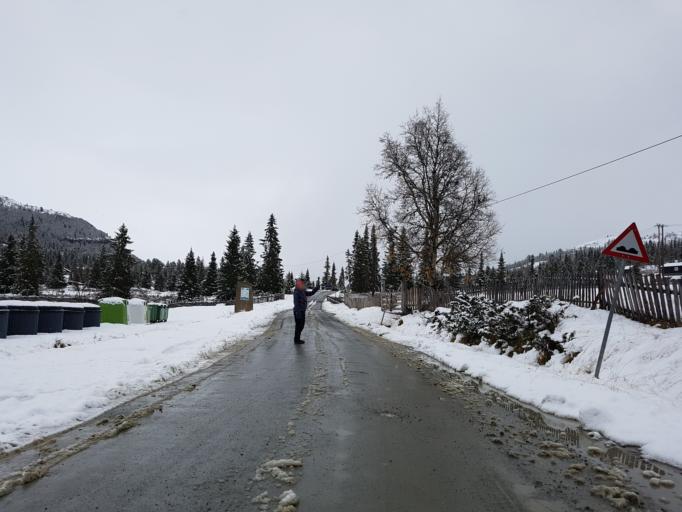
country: NO
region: Oppland
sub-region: Sel
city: Otta
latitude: 61.8075
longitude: 9.6841
